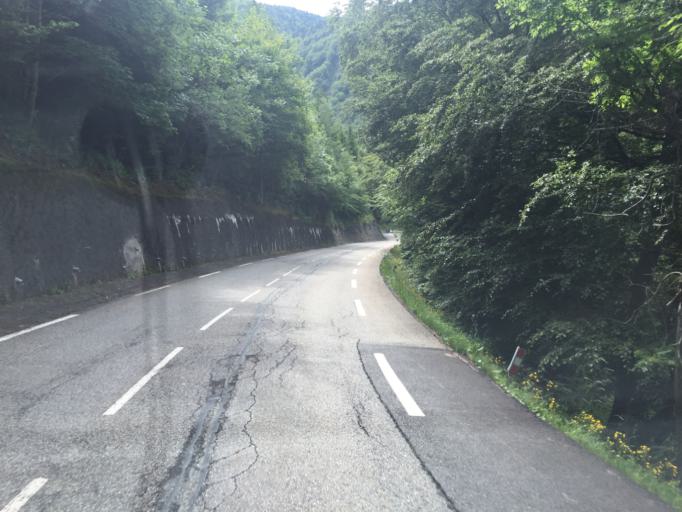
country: FR
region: Rhone-Alpes
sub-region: Departement de la Savoie
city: Saint-Baldoph
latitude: 45.4999
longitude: 5.9187
